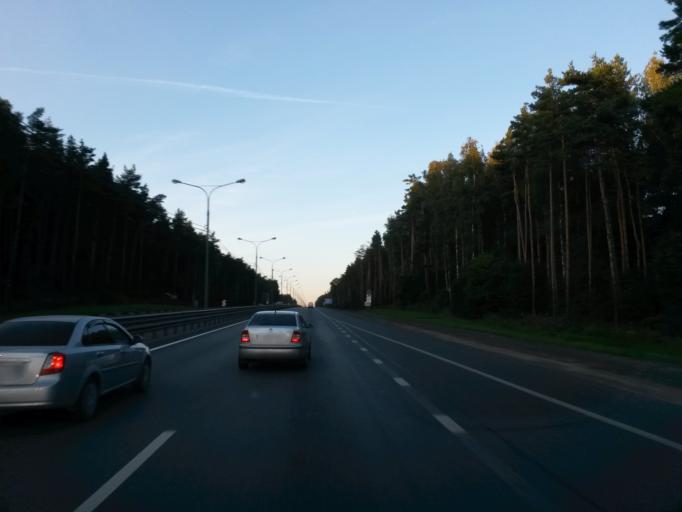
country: RU
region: Moskovskaya
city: Kostino
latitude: 56.0413
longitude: 37.8927
